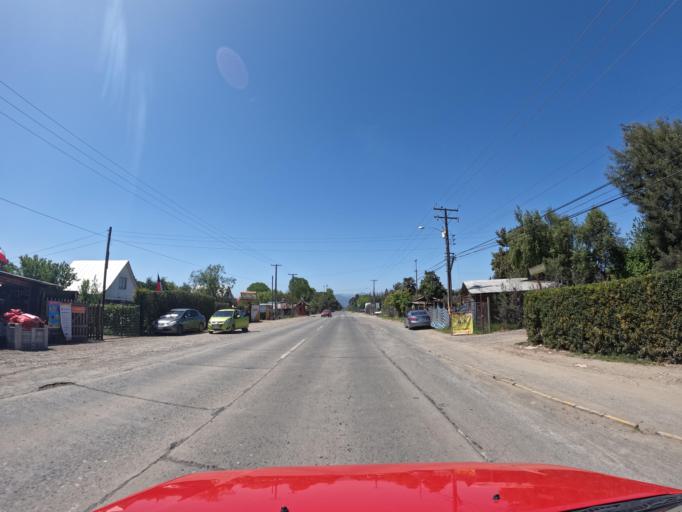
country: CL
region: Maule
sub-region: Provincia de Linares
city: Linares
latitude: -35.8320
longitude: -71.5260
